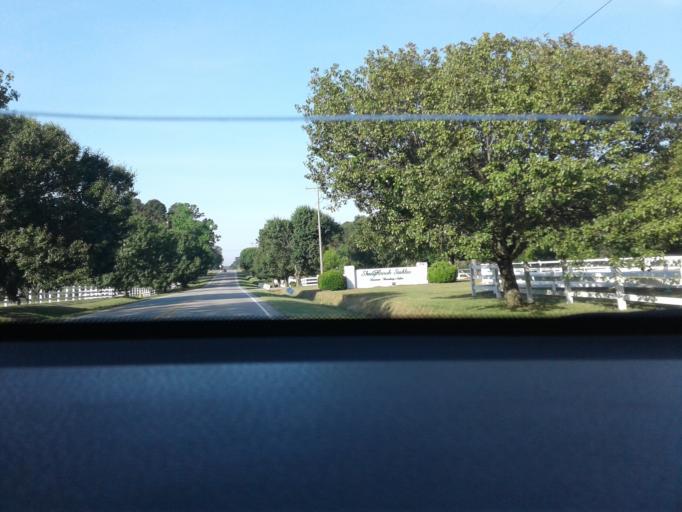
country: US
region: North Carolina
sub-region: Harnett County
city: Dunn
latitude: 35.3400
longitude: -78.5860
